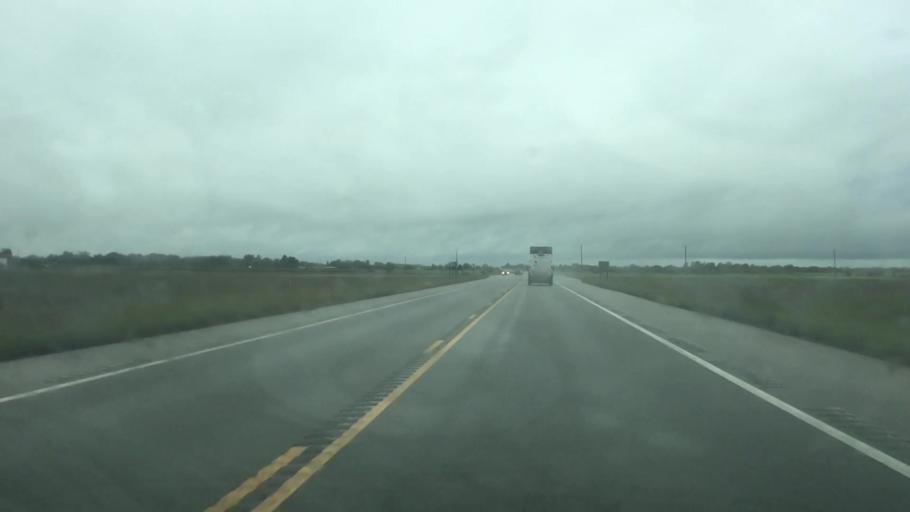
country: US
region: Kansas
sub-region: Allen County
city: Iola
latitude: 38.0835
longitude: -95.3688
